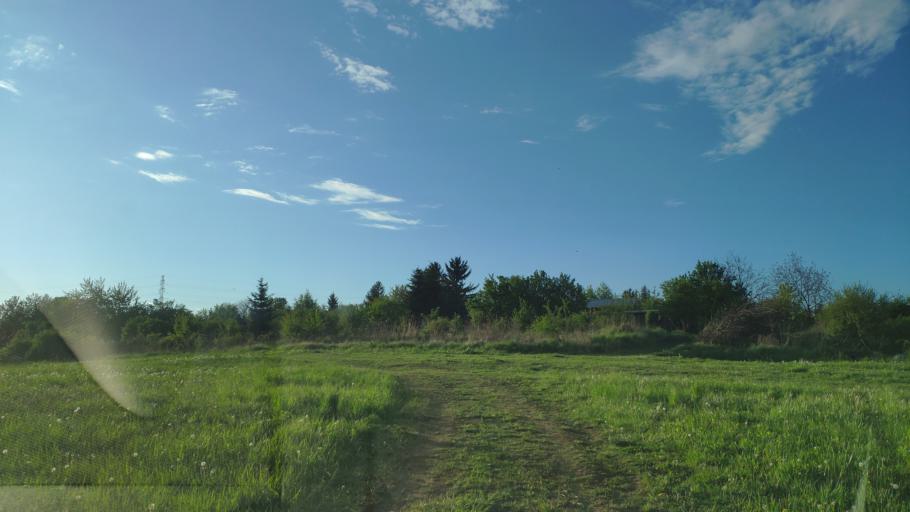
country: SK
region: Kosicky
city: Kosice
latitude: 48.7252
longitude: 21.3087
